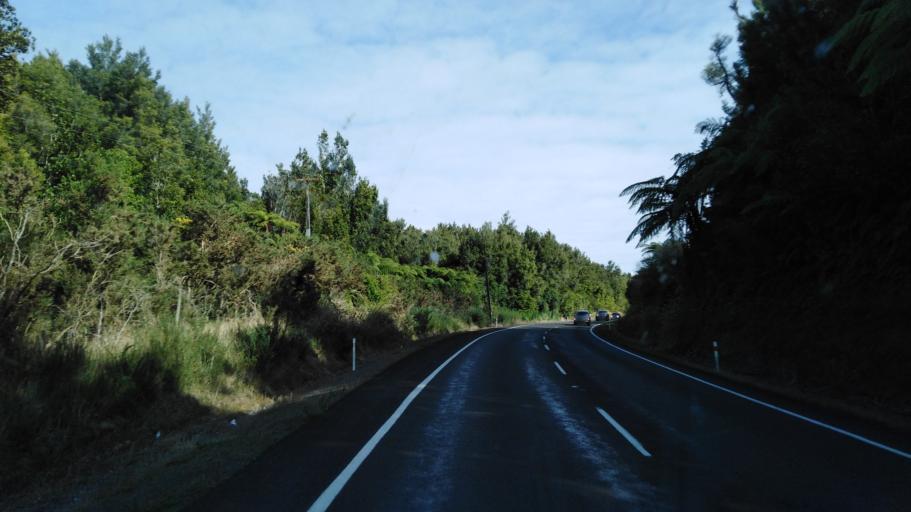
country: NZ
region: Bay of Plenty
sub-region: Tauranga City
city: Tauranga
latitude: -37.8694
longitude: 176.1331
